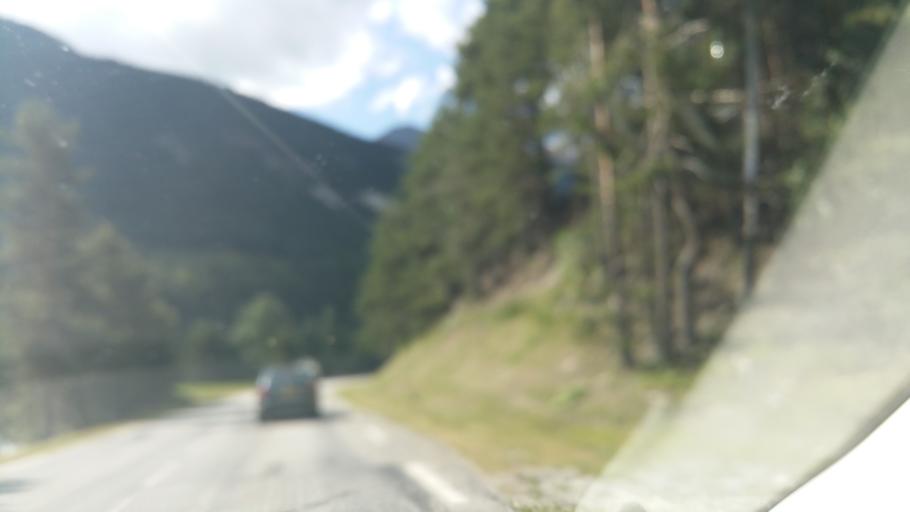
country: FR
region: Rhone-Alpes
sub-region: Departement de la Savoie
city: Modane
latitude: 45.2420
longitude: 6.7926
